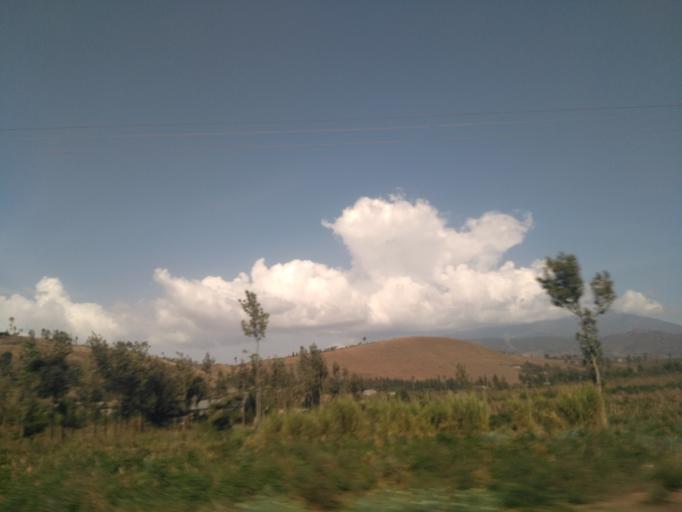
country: TZ
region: Arusha
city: Arusha
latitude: -3.2262
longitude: 36.6068
